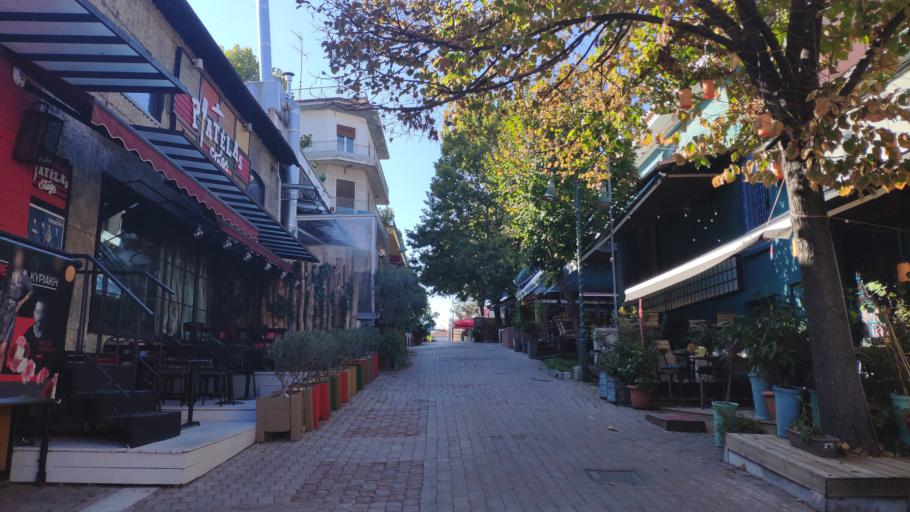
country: GR
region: Thessaly
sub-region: Nomos Larisis
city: Larisa
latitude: 39.6407
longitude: 22.4173
